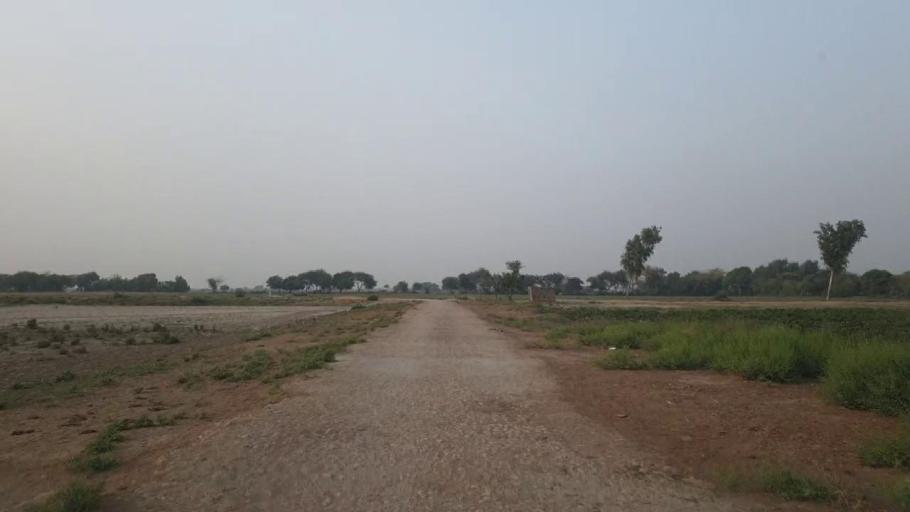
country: PK
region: Sindh
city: Mirpur Batoro
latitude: 24.6622
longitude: 68.3844
